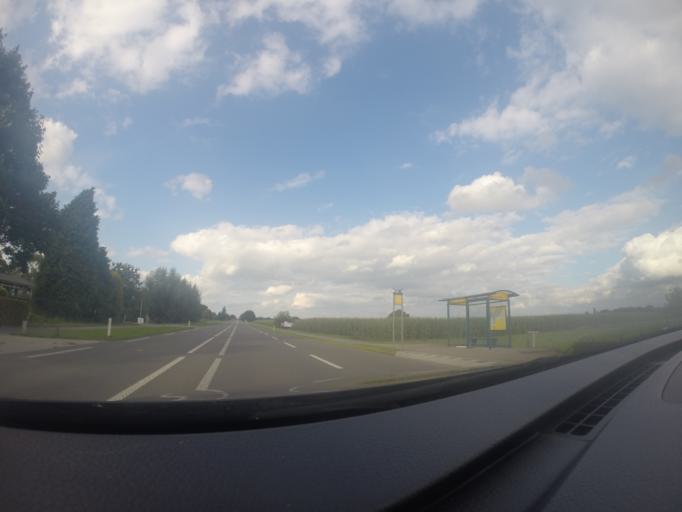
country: NL
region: Gelderland
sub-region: Gemeente Bronckhorst
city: Baak
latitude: 52.0445
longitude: 6.2200
